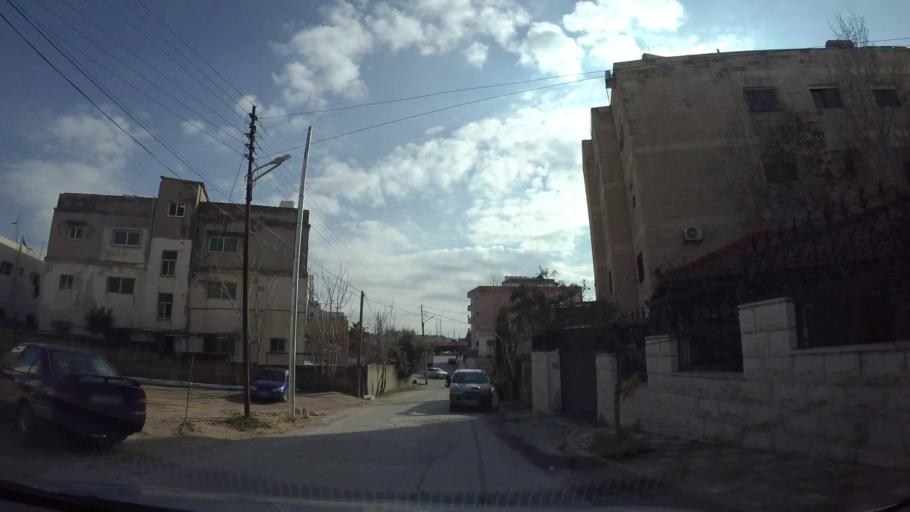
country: JO
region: Amman
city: Al Jubayhah
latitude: 32.0199
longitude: 35.8492
